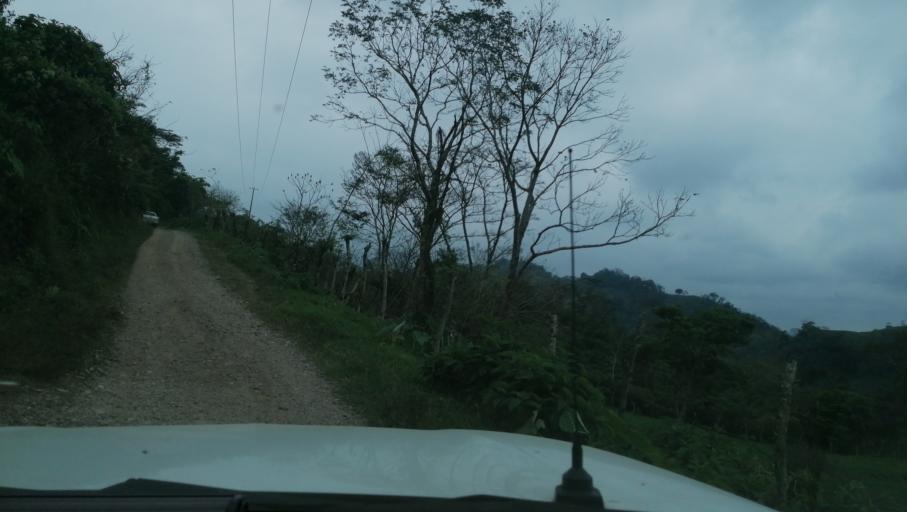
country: MX
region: Chiapas
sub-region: Francisco Leon
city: San Miguel la Sardina
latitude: 17.3357
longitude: -93.3138
